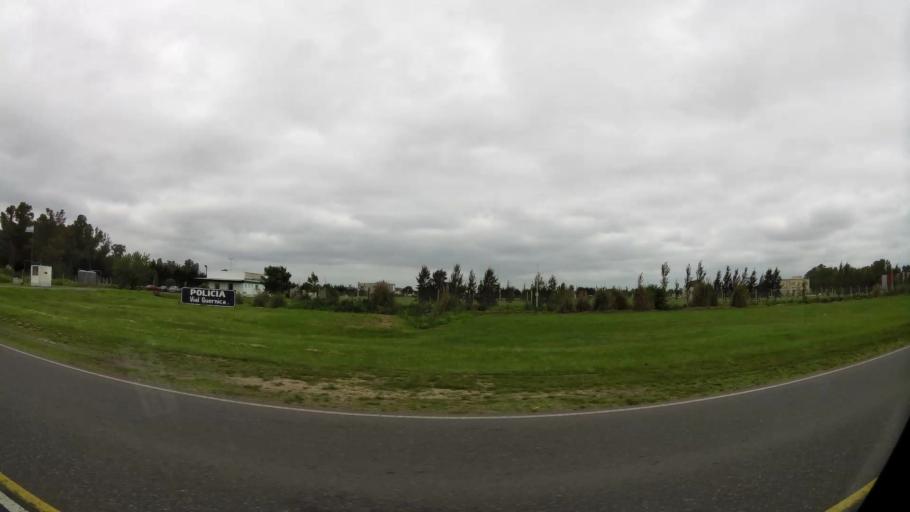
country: AR
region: Buenos Aires
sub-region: Partido de San Vicente
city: San Vicente
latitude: -34.9983
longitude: -58.4698
